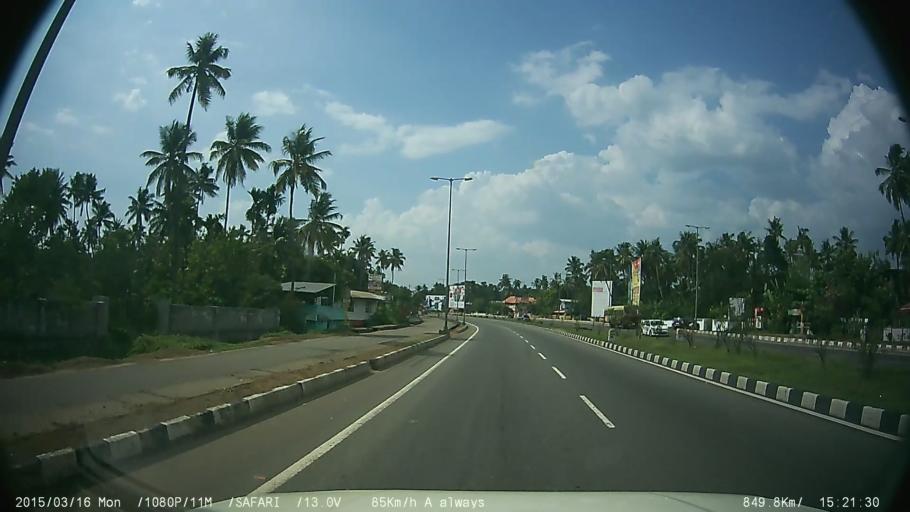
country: IN
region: Kerala
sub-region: Thrissur District
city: Kizhake Chalakudi
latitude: 10.3661
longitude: 76.3146
